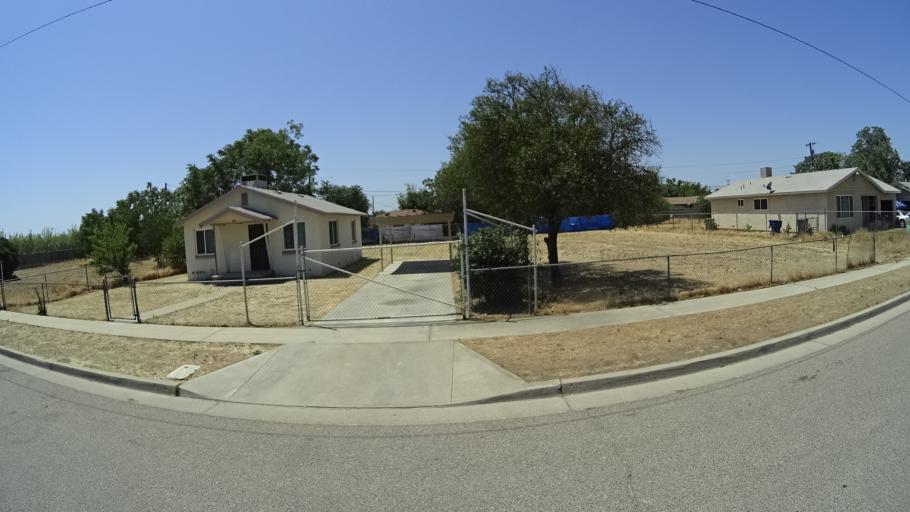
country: US
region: California
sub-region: Fresno County
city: West Park
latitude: 36.7096
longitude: -119.8072
